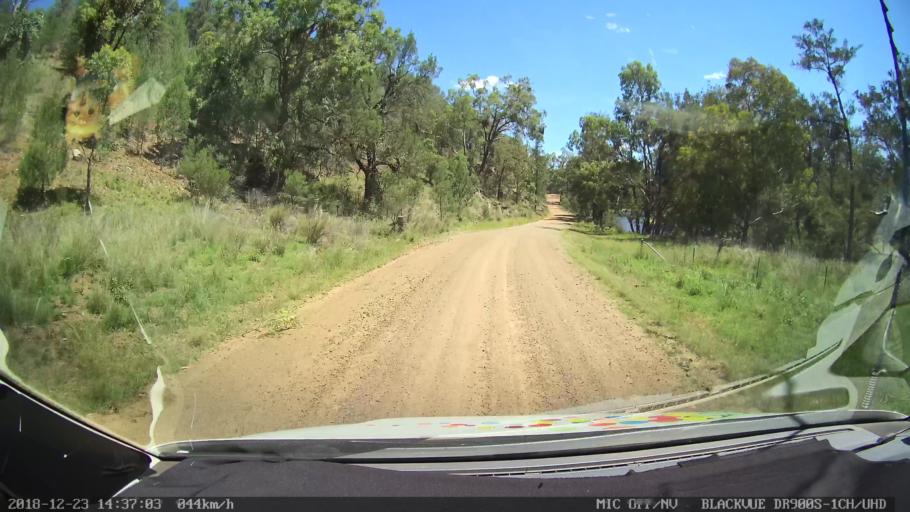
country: AU
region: New South Wales
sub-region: Tamworth Municipality
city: Manilla
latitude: -30.6134
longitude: 150.9086
